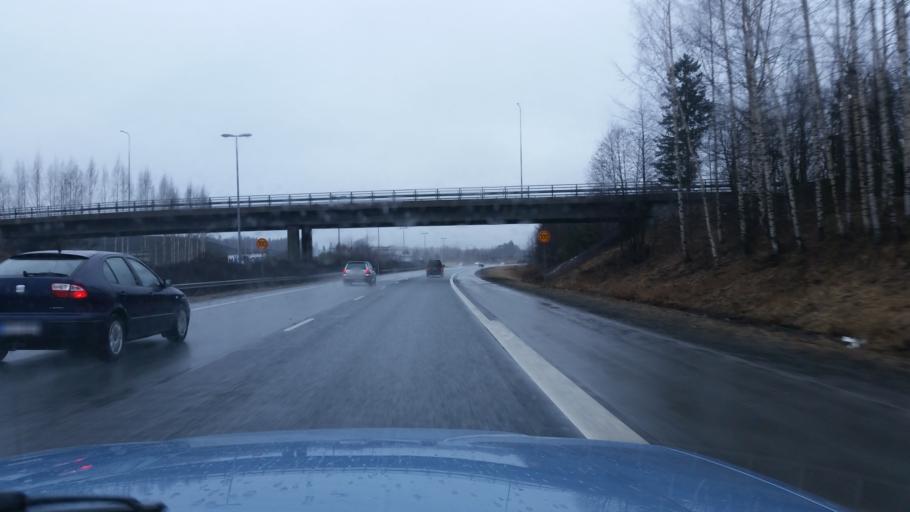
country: FI
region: Haeme
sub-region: Haemeenlinna
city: Haemeenlinna
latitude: 61.0148
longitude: 24.4132
